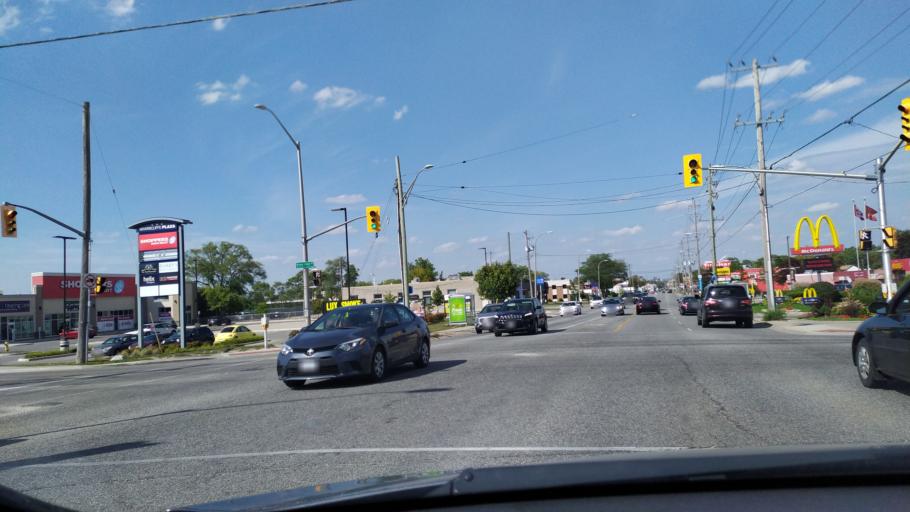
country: CA
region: Ontario
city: London
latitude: 42.9591
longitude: -81.2610
